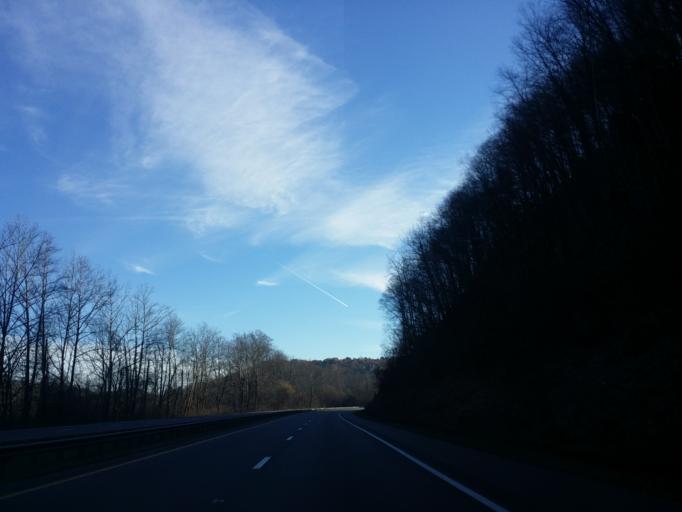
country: US
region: North Carolina
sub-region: McDowell County
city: West Marion
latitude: 35.6405
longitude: -82.1224
